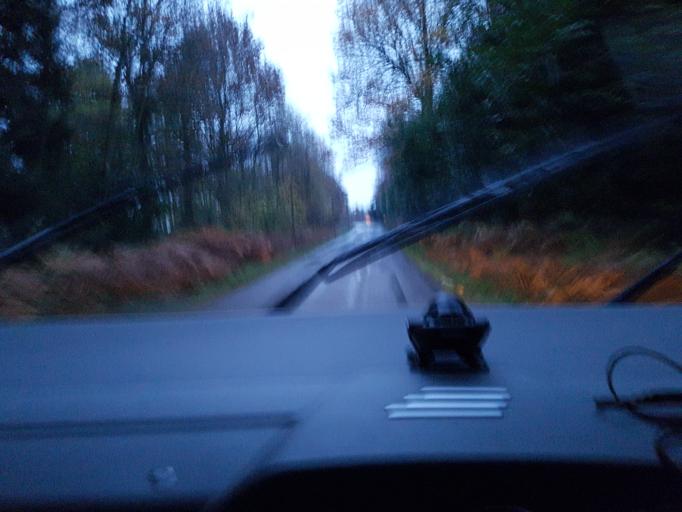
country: FR
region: Brittany
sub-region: Departement d'Ille-et-Vilaine
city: Montreuil-sous-Perouse
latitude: 48.1848
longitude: -1.2923
